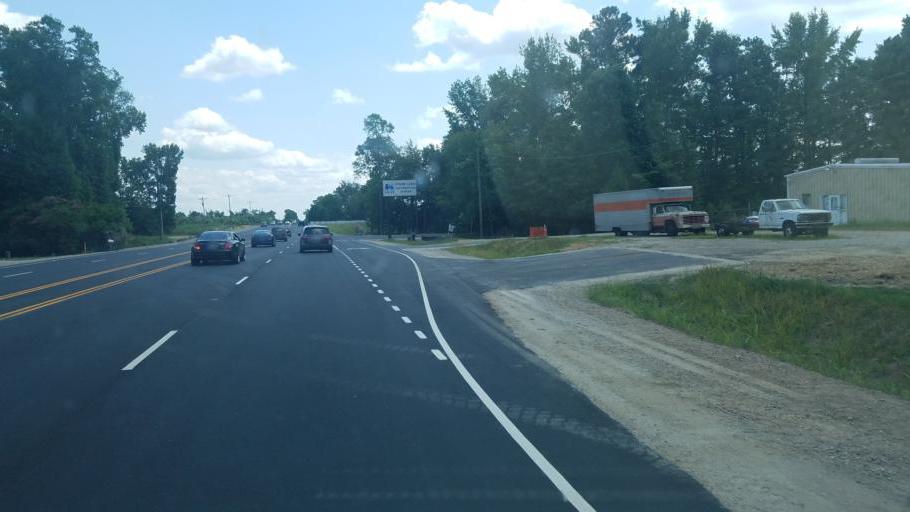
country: US
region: Virginia
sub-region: Prince George County
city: Prince George
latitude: 37.1641
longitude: -77.2882
